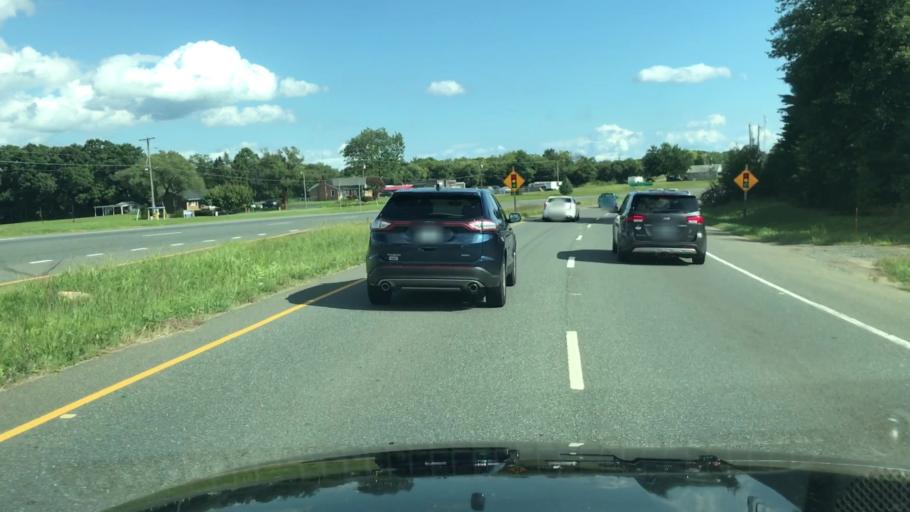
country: US
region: Virginia
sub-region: Stafford County
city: Falmouth
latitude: 38.3688
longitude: -77.5237
